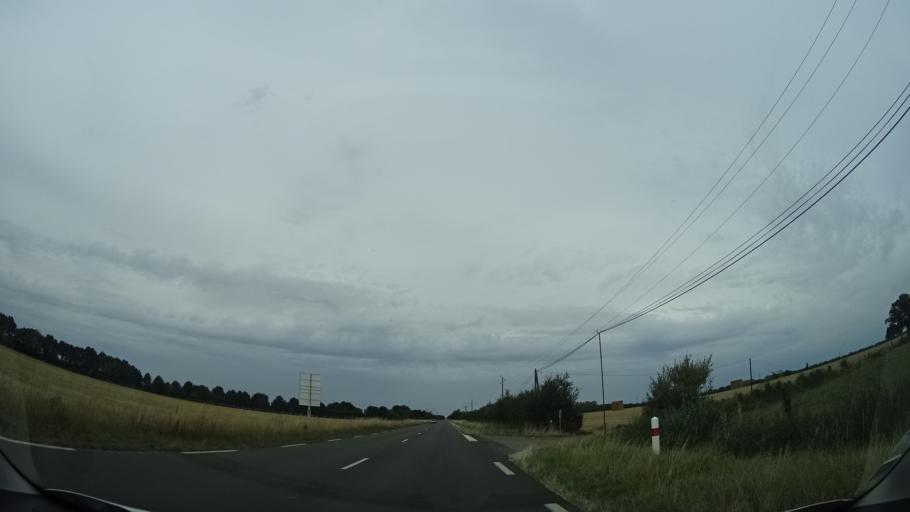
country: FR
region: Pays de la Loire
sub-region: Departement de la Mayenne
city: Meslay-du-Maine
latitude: 47.9711
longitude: -0.5919
